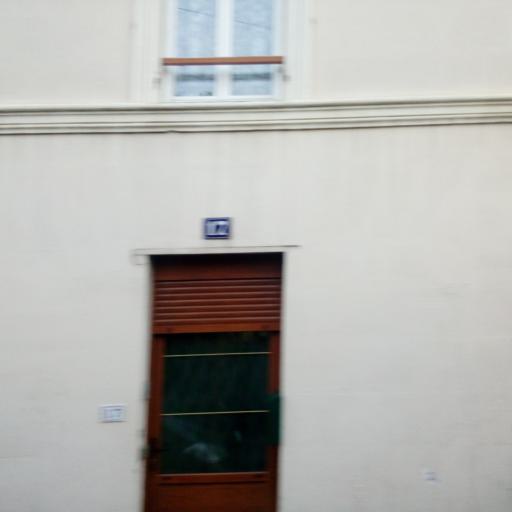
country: FR
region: Poitou-Charentes
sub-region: Departement de la Charente-Maritime
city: Jonzac
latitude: 45.4476
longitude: -0.4351
